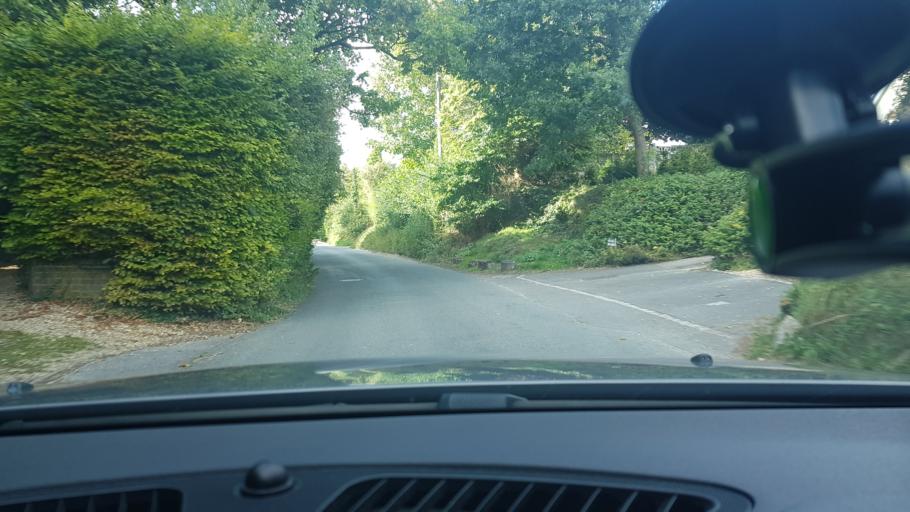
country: GB
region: England
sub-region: Wiltshire
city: Shalbourne
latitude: 51.3691
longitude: -1.5457
